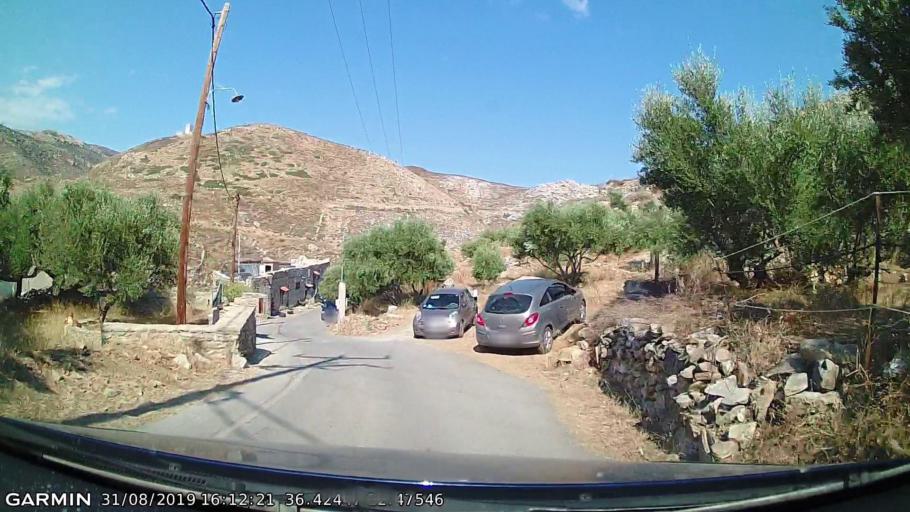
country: GR
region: Peloponnese
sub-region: Nomos Lakonias
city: Gytheio
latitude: 36.4245
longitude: 22.4754
